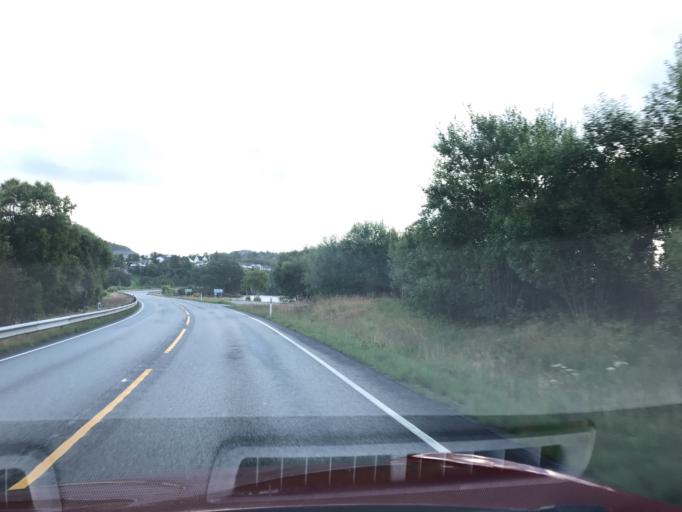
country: NO
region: Hordaland
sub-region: Sveio
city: Sveio
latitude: 59.5381
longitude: 5.3464
